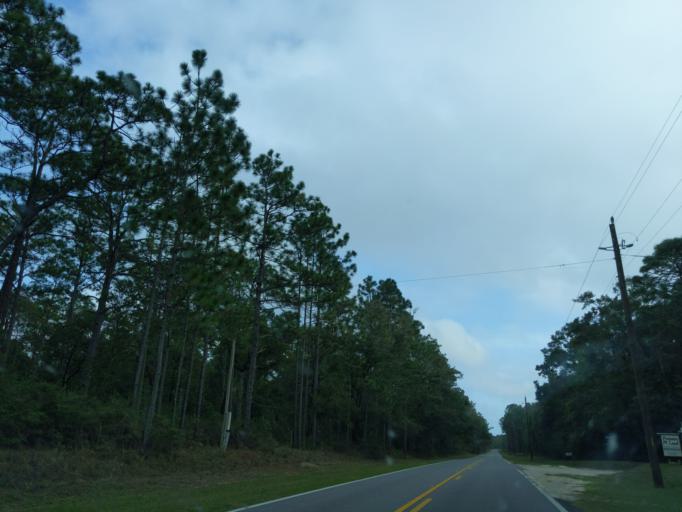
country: US
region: Florida
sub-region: Wakulla County
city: Crawfordville
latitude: 30.1186
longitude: -84.3138
